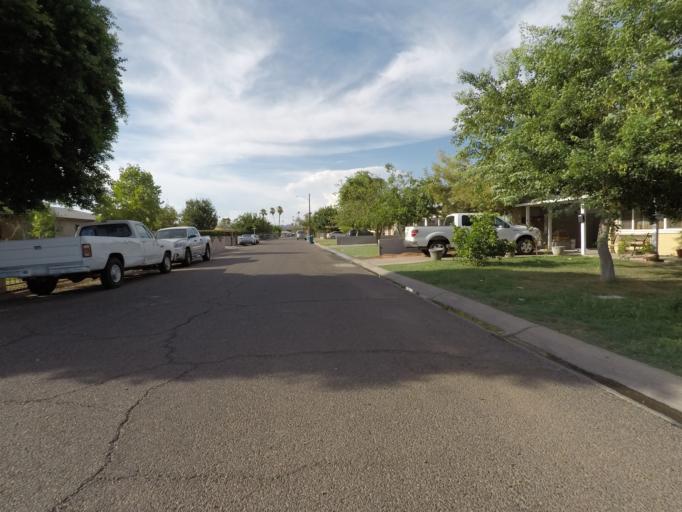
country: US
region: Arizona
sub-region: Maricopa County
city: Phoenix
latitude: 33.4618
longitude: -112.0084
